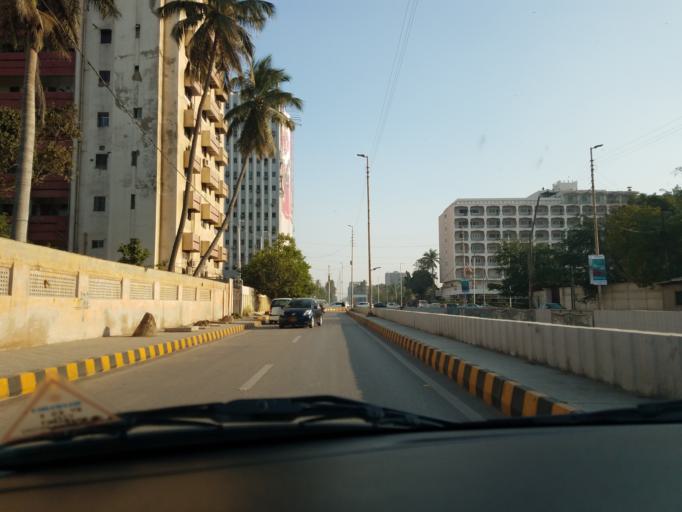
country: PK
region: Sindh
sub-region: Karachi District
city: Karachi
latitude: 24.8532
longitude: 67.0339
